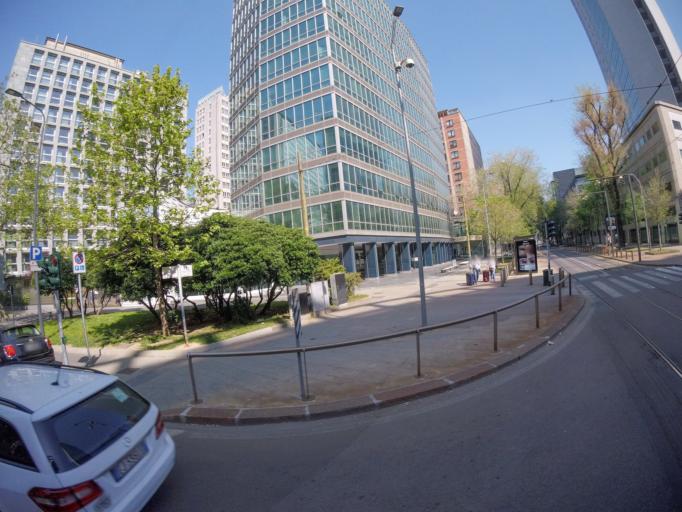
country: IT
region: Lombardy
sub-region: Citta metropolitana di Milano
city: Milano
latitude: 45.4840
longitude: 9.2000
